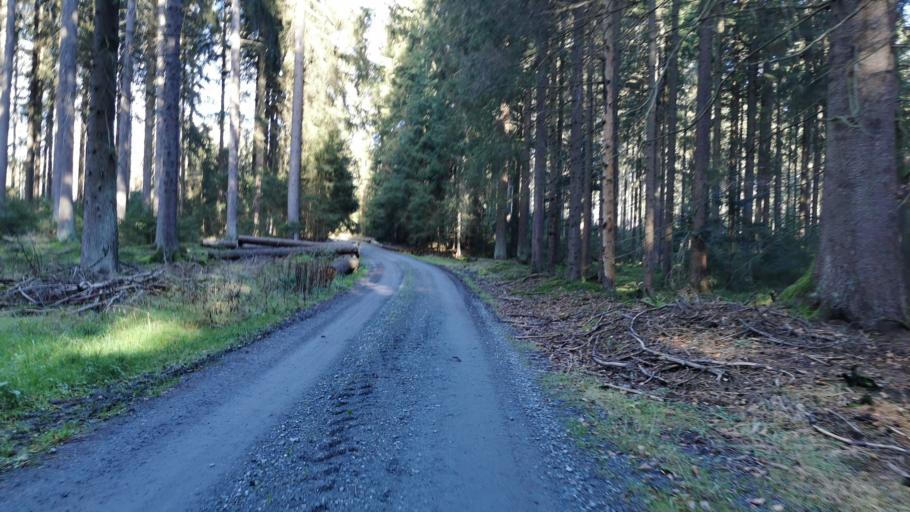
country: DE
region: Bavaria
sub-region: Upper Franconia
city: Reichenbach
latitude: 50.4203
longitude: 11.4363
